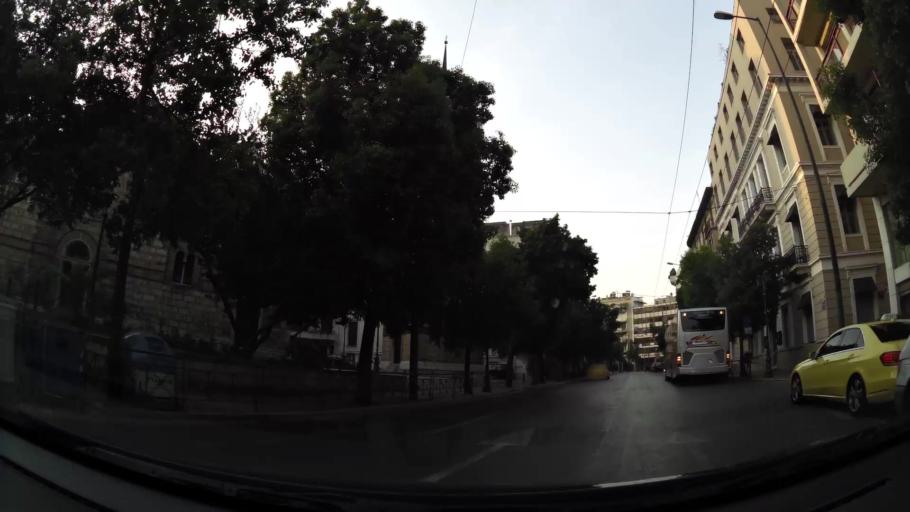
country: GR
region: Attica
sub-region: Nomarchia Athinas
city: Athens
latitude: 37.9733
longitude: 23.7337
